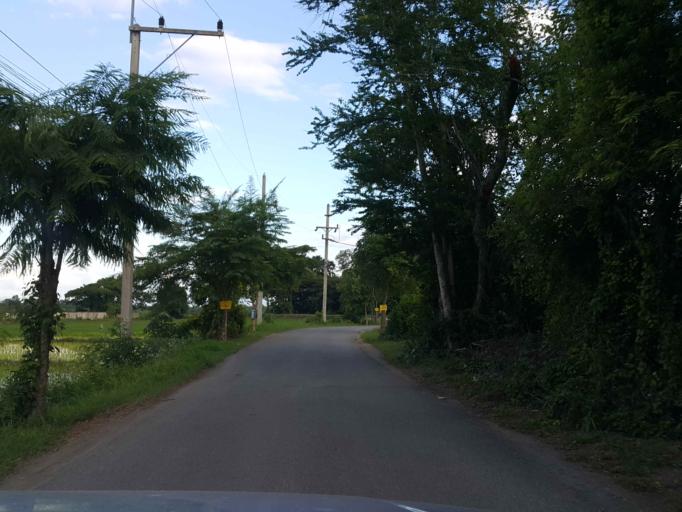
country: TH
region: Chiang Mai
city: San Sai
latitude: 18.9122
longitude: 98.9775
